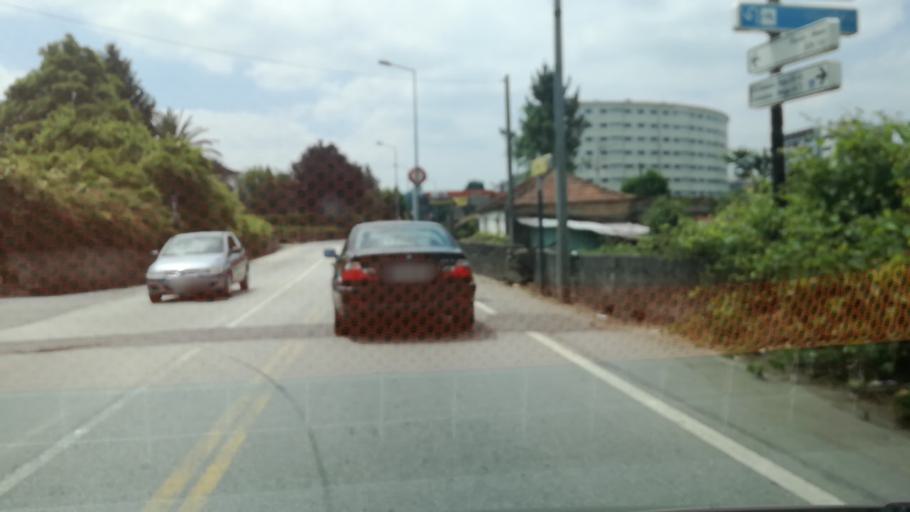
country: PT
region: Porto
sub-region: Trofa
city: Bougado
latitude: 41.3443
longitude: -8.5566
